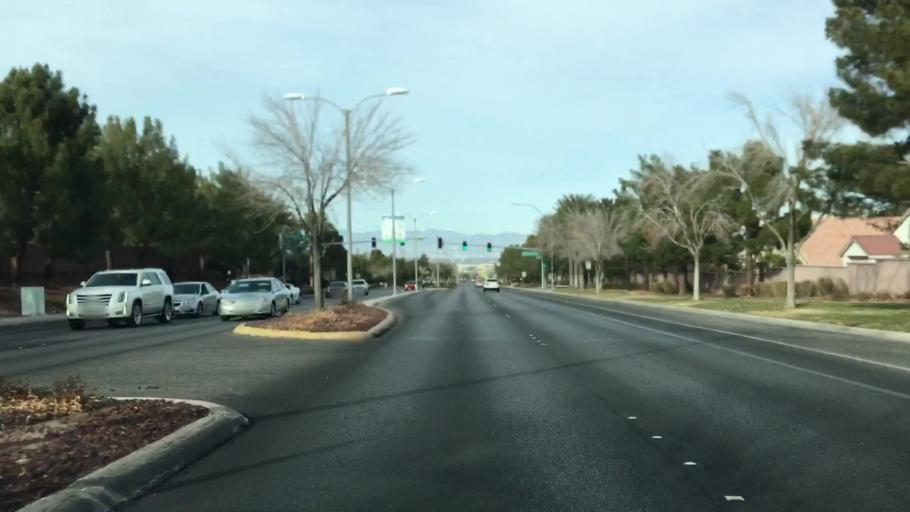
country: US
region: Nevada
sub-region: Clark County
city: Whitney
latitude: 36.0136
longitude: -115.0830
